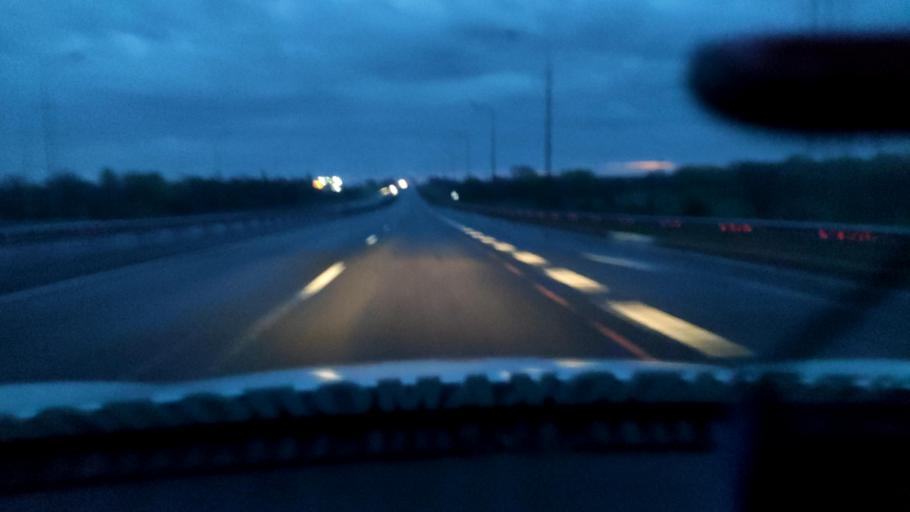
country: RU
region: Rostov
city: Glubokiy
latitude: 48.5376
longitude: 40.3457
